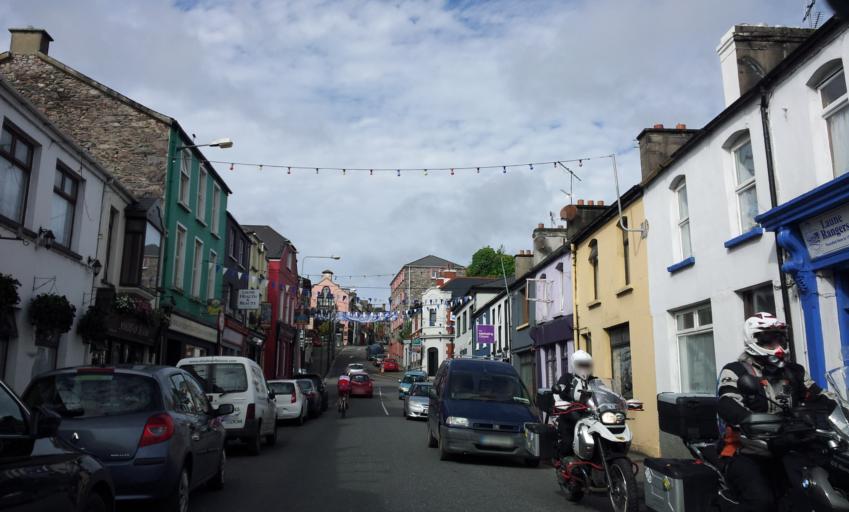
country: IE
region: Munster
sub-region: Ciarrai
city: Killorglin
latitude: 52.1064
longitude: -9.7838
